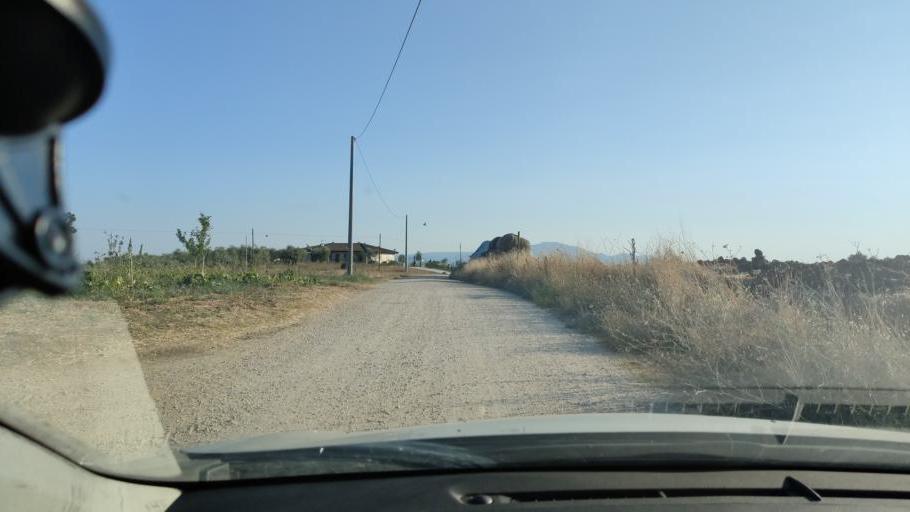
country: IT
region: Umbria
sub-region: Provincia di Terni
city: Giove
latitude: 42.5387
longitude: 12.3636
